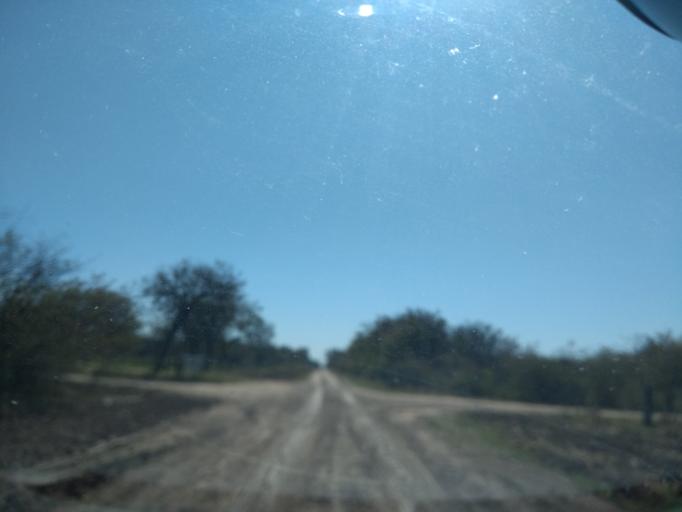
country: AR
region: Chaco
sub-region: Departamento de Quitilipi
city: Quitilipi
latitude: -26.7322
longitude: -60.2323
